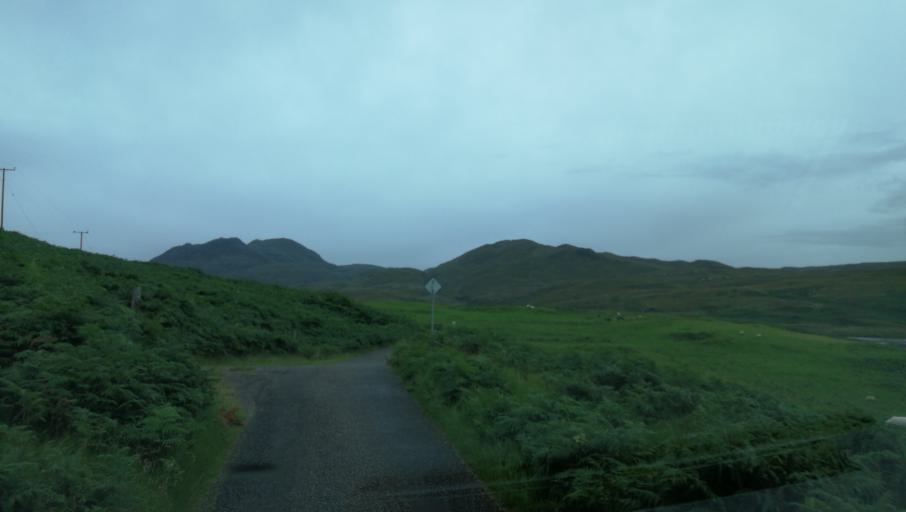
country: GB
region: Scotland
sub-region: Argyll and Bute
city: Isle Of Mull
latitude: 56.7237
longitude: -6.1958
